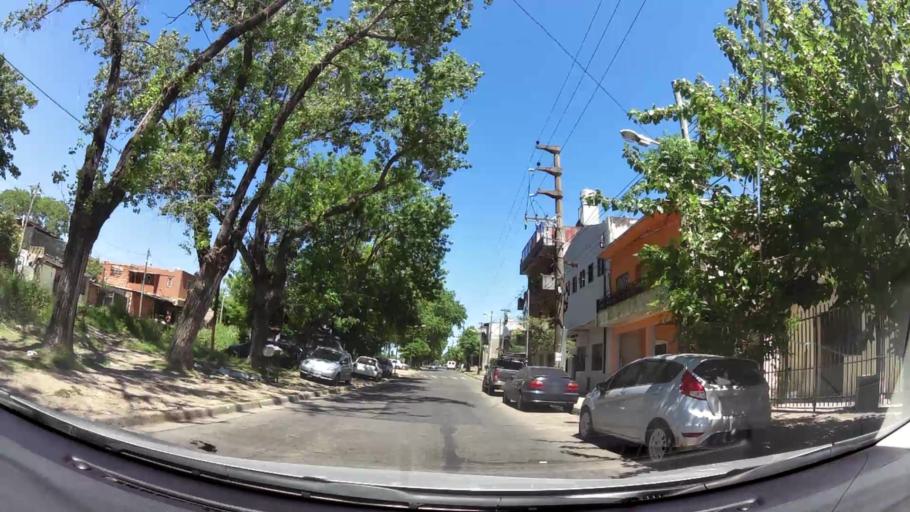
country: AR
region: Buenos Aires
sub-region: Partido de Tigre
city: Tigre
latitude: -34.4624
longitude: -58.5550
